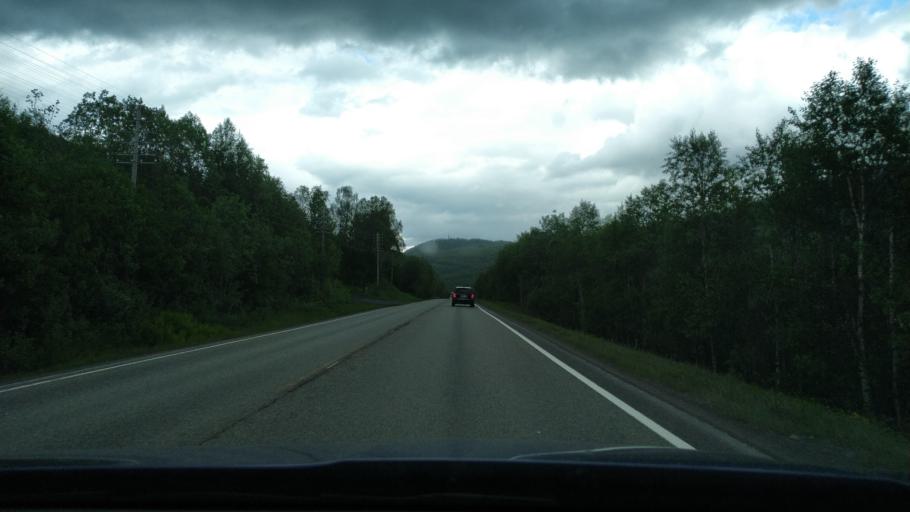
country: NO
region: Troms
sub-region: Malselv
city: Moen
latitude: 68.9787
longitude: 18.5039
